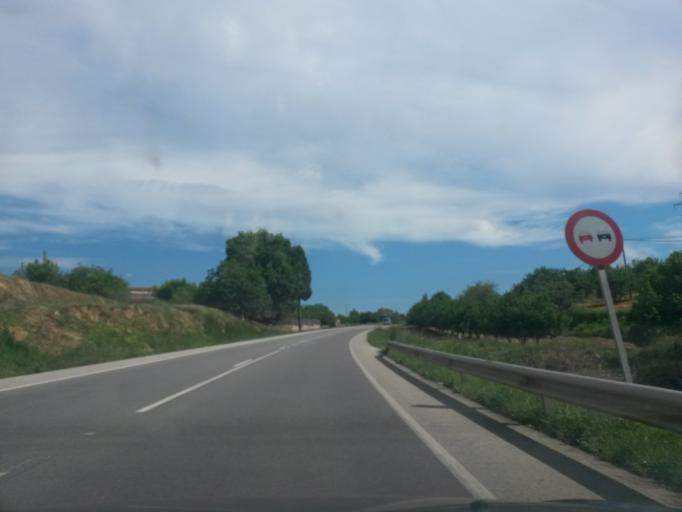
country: ES
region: Catalonia
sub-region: Provincia de Girona
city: Angles
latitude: 41.9301
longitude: 2.6487
